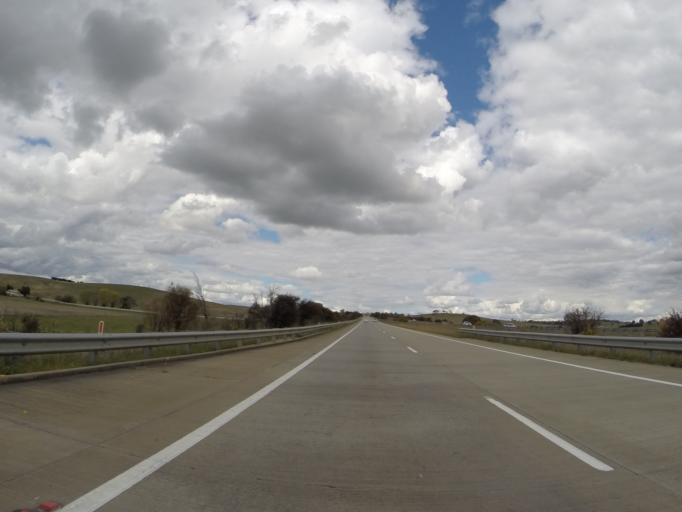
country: AU
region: New South Wales
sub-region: Yass Valley
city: Gundaroo
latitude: -34.7921
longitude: 149.2676
